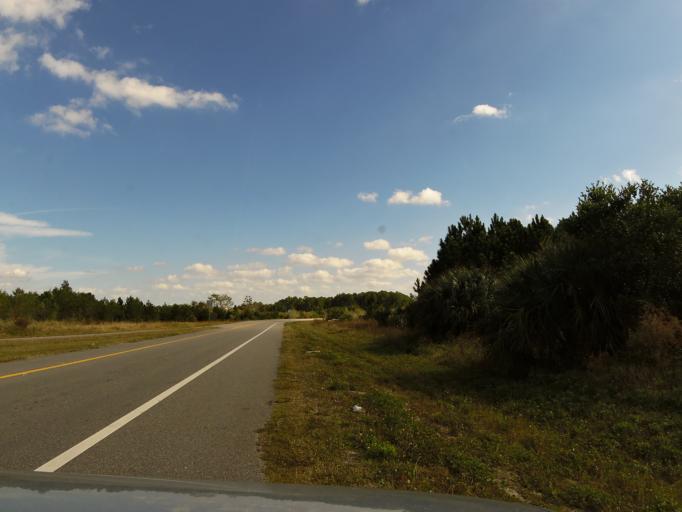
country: US
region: Florida
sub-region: Duval County
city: Jacksonville
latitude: 30.4188
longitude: -81.6369
